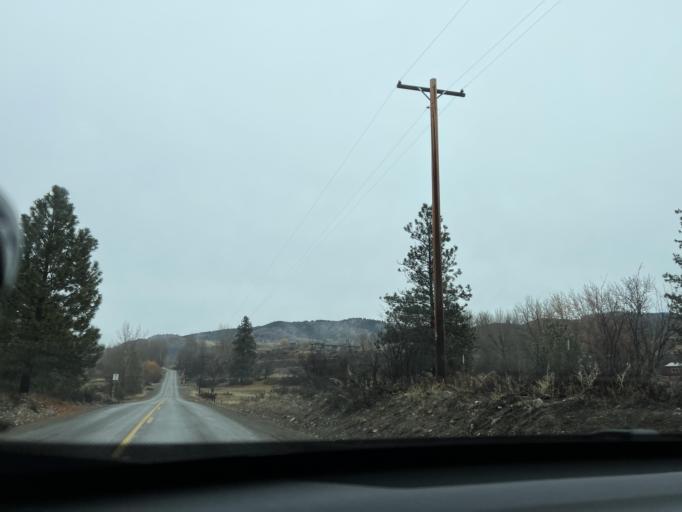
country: US
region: Washington
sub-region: Okanogan County
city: Brewster
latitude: 48.4972
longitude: -120.1756
